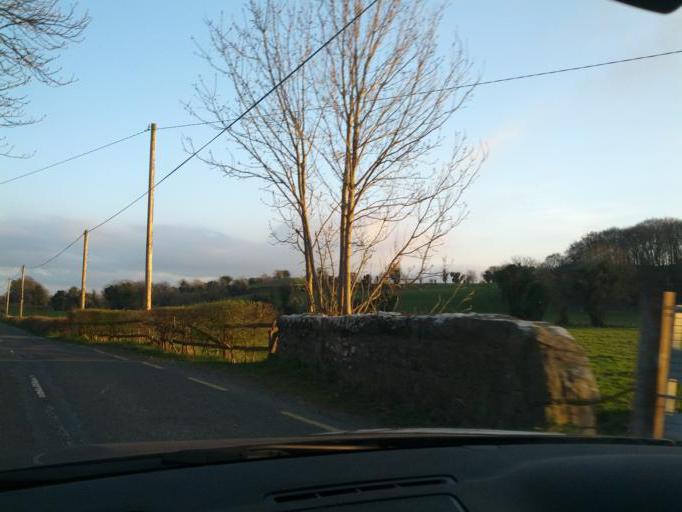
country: IE
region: Munster
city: Nenagh Bridge
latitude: 52.9578
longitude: -8.2358
